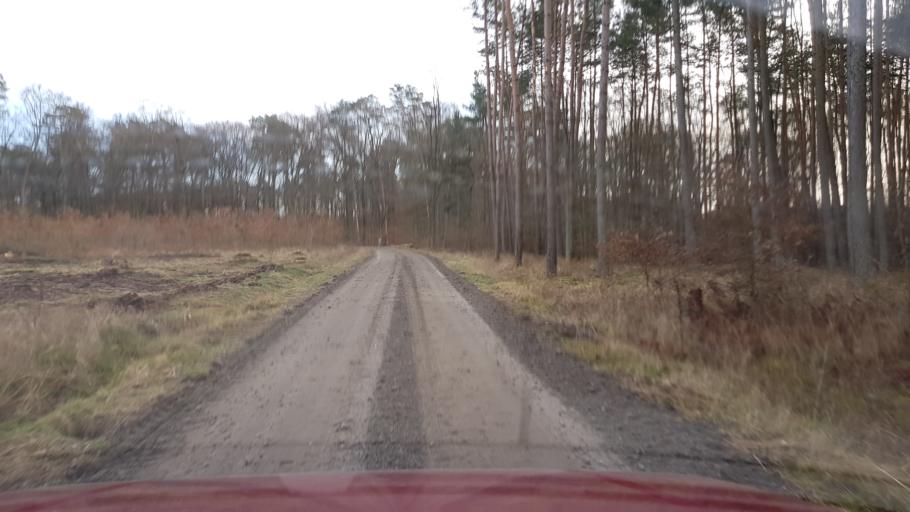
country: PL
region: Lubusz
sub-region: Powiat strzelecko-drezdenecki
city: Strzelce Krajenskie
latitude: 52.9109
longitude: 15.3821
